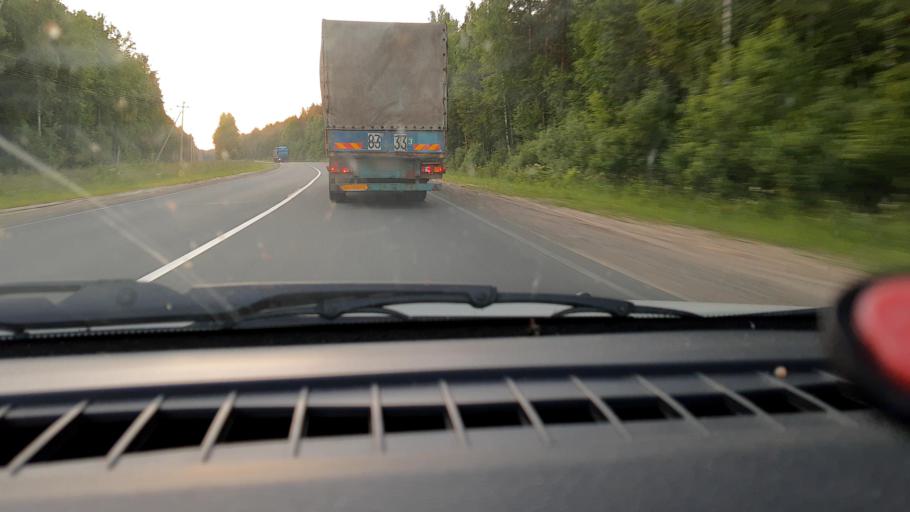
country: RU
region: Nizjnij Novgorod
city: Uren'
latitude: 57.3743
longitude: 45.6928
